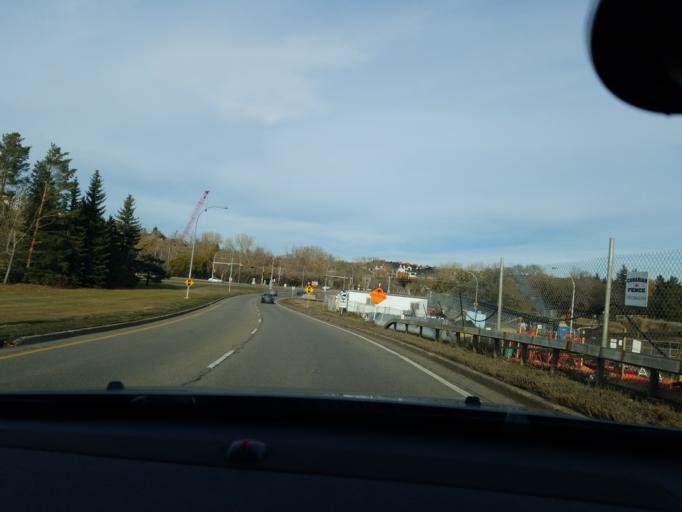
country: CA
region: Alberta
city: Edmonton
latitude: 53.5364
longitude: -113.4804
